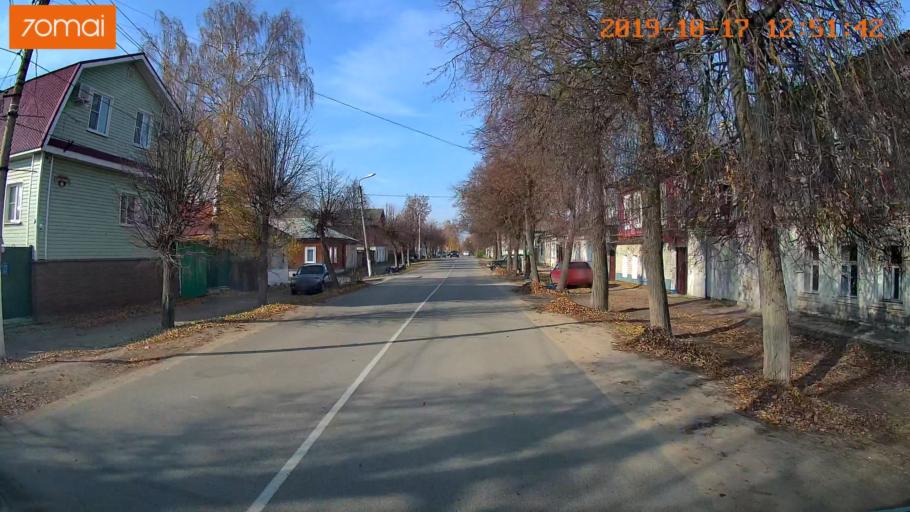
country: RU
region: Rjazan
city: Kasimov
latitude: 54.9414
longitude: 41.3910
